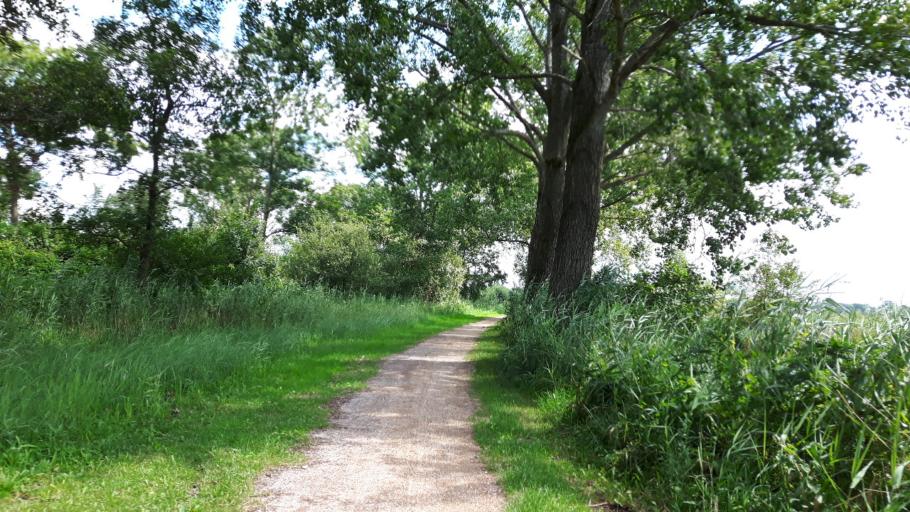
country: NL
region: Utrecht
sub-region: Stichtse Vecht
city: Breukelen
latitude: 52.1854
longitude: 4.9555
